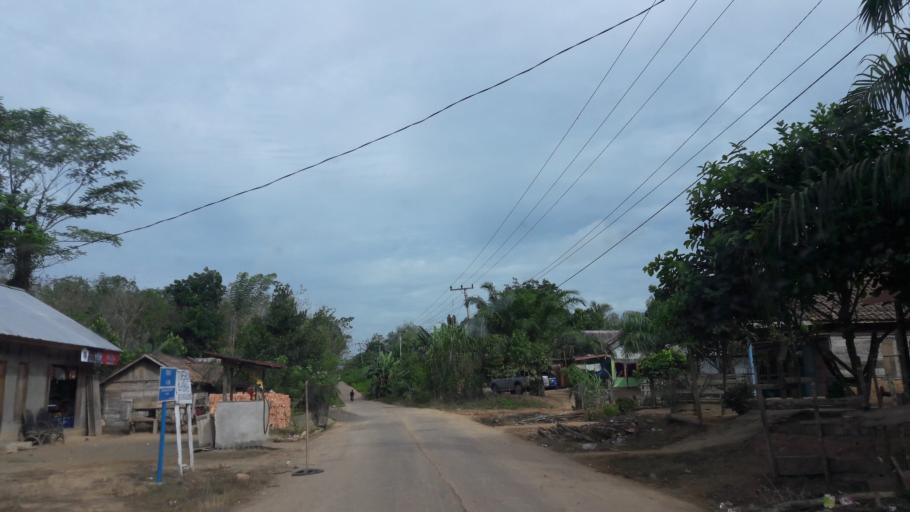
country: ID
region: South Sumatra
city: Gunungmegang Dalam
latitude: -3.2870
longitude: 103.7201
